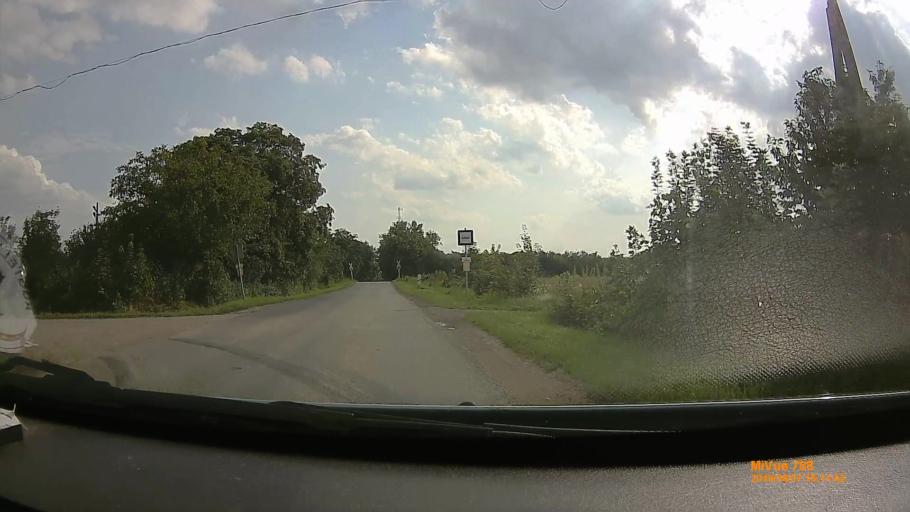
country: HU
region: Borsod-Abauj-Zemplen
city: Gonc
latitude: 48.4734
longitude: 21.2577
